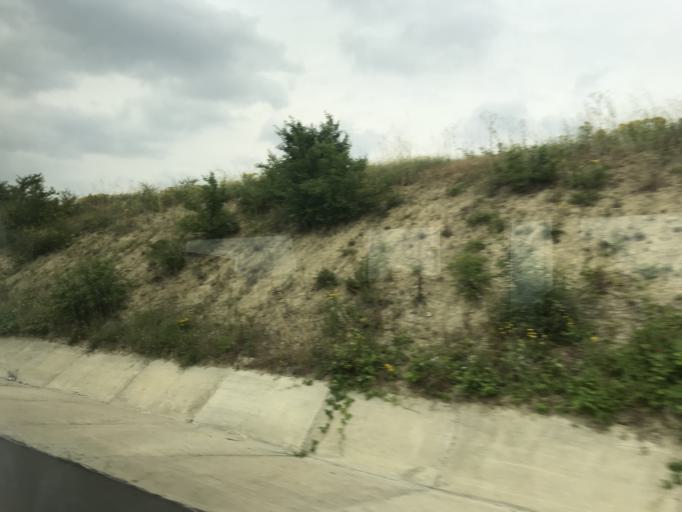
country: TR
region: Tekirdag
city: Malkara
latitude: 40.8796
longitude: 26.8798
